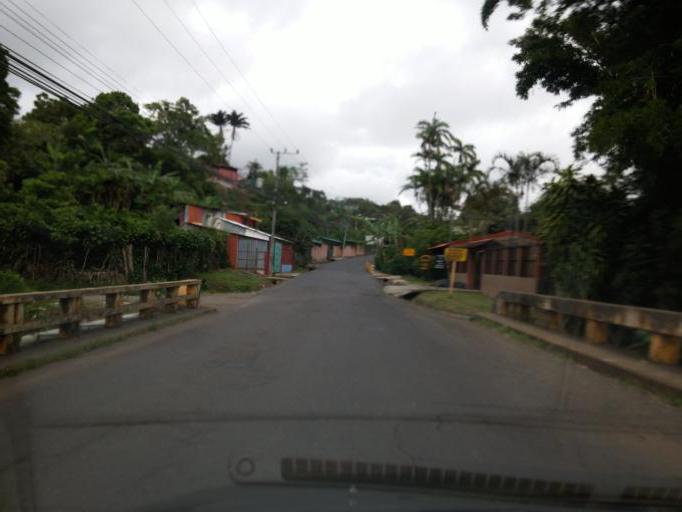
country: CR
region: Heredia
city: Santo Domingo
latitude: 10.0397
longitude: -84.1424
